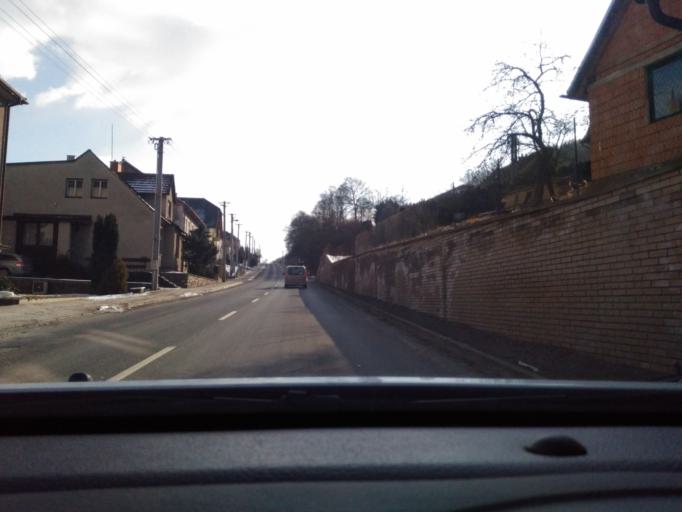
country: CZ
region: South Moravian
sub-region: Okres Brno-Venkov
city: Nedvedice
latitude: 49.4214
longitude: 16.3527
